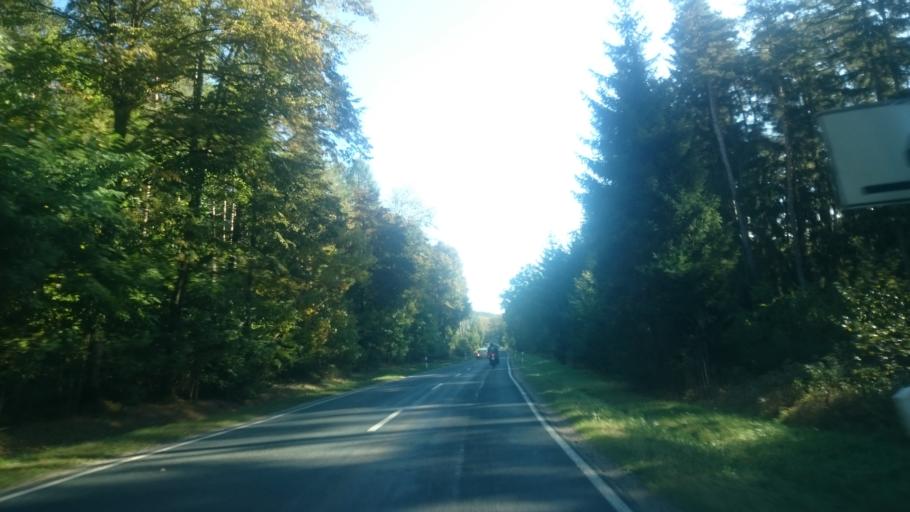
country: DE
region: Bavaria
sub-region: Regierungsbezirk Mittelfranken
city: Rottenbach
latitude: 49.1330
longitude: 11.0524
